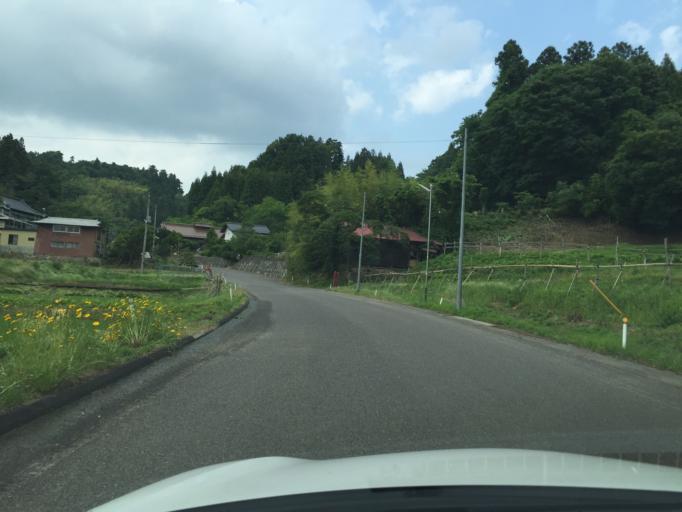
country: JP
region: Fukushima
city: Miharu
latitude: 37.3638
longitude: 140.4895
